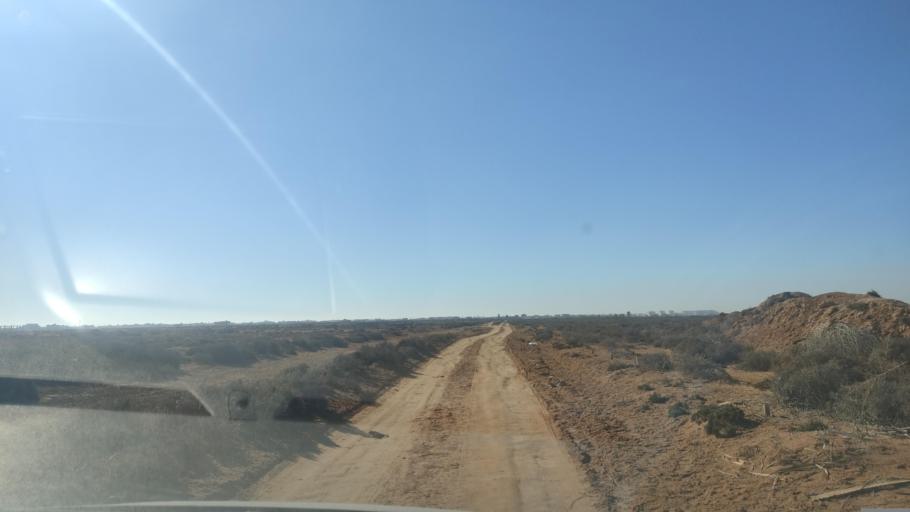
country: TN
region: Safaqis
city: Al Qarmadah
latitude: 34.8180
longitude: 10.8559
